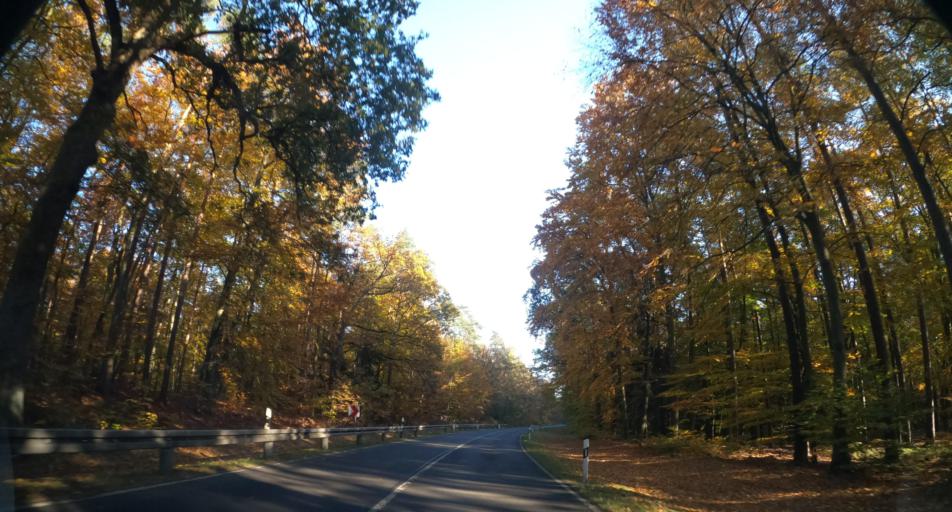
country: DE
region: Mecklenburg-Vorpommern
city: Ahlbeck
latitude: 53.6759
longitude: 14.1493
